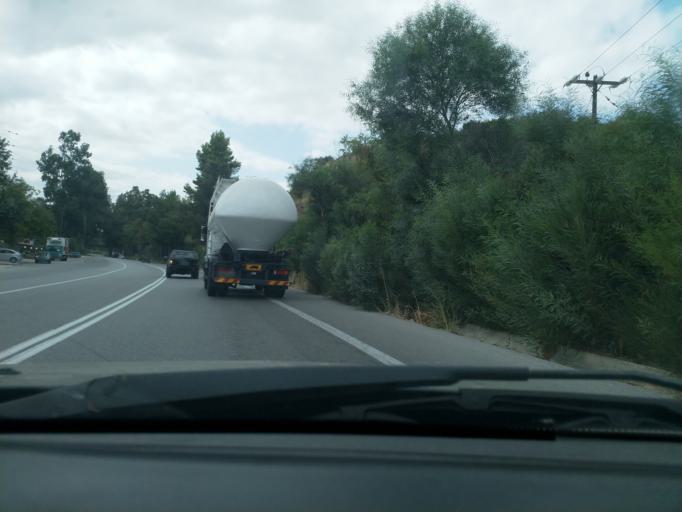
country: GR
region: Crete
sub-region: Nomos Chanias
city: Georgioupolis
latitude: 35.3784
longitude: 24.2054
